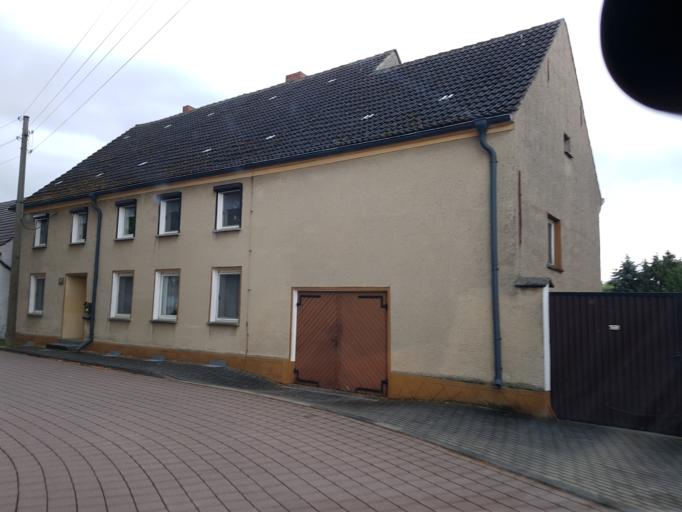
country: DE
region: Saxony-Anhalt
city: Seyda
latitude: 51.9031
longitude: 12.9413
